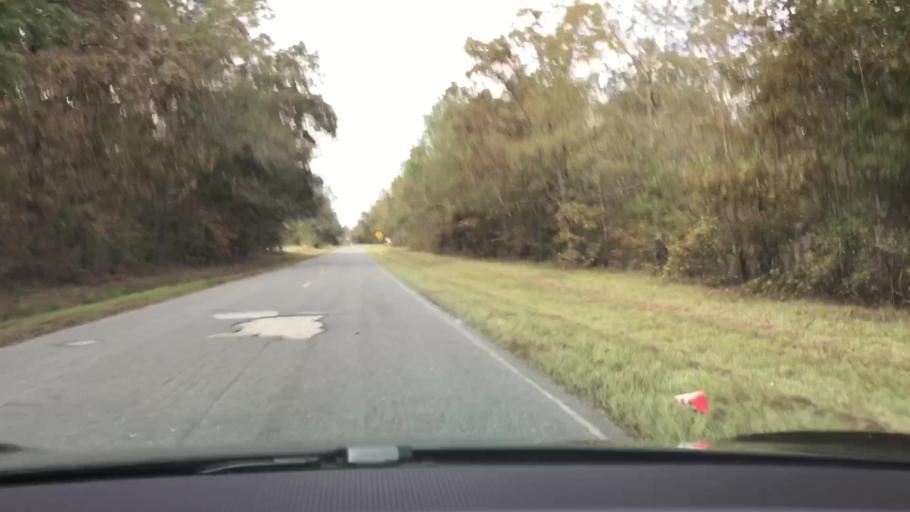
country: US
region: Georgia
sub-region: Jefferson County
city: Wadley
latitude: 32.7994
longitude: -82.3623
